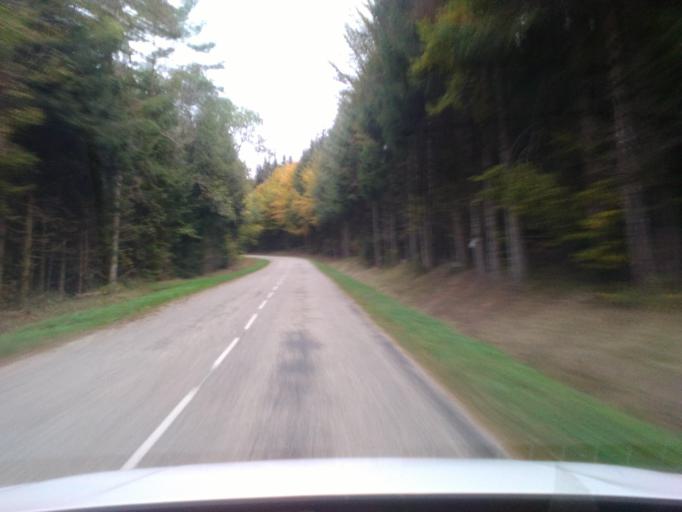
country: FR
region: Lorraine
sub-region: Departement des Vosges
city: Senones
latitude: 48.3695
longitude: 7.1055
